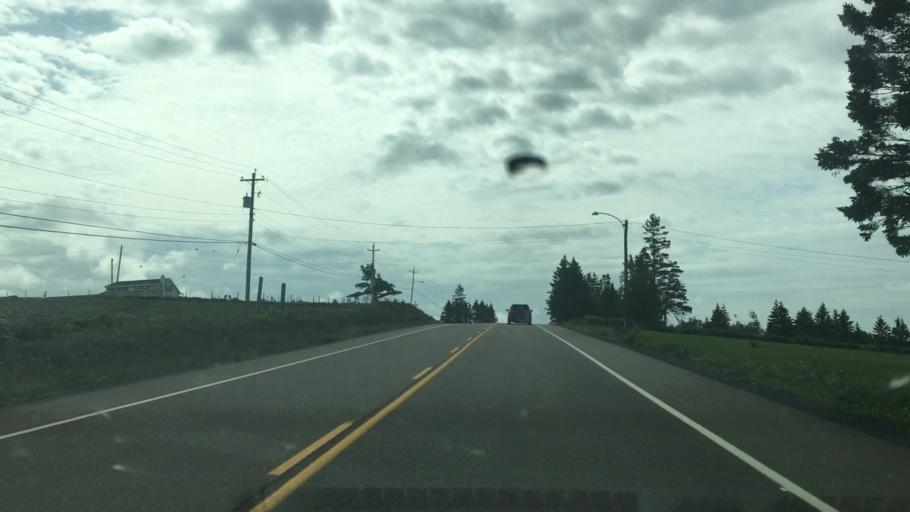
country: CA
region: Nova Scotia
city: Princeville
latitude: 45.6985
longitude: -60.7366
